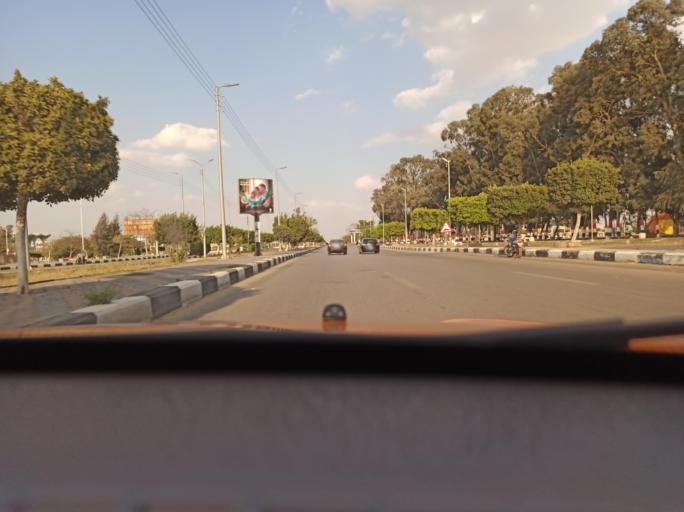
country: EG
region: Al Isma'iliyah
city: Ismailia
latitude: 30.6178
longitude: 32.2674
